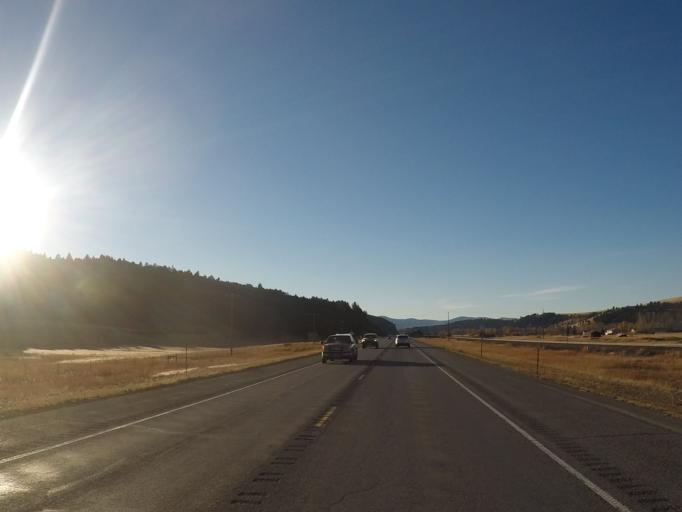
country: US
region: Montana
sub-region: Lewis and Clark County
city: Helena West Side
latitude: 46.5623
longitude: -112.4348
